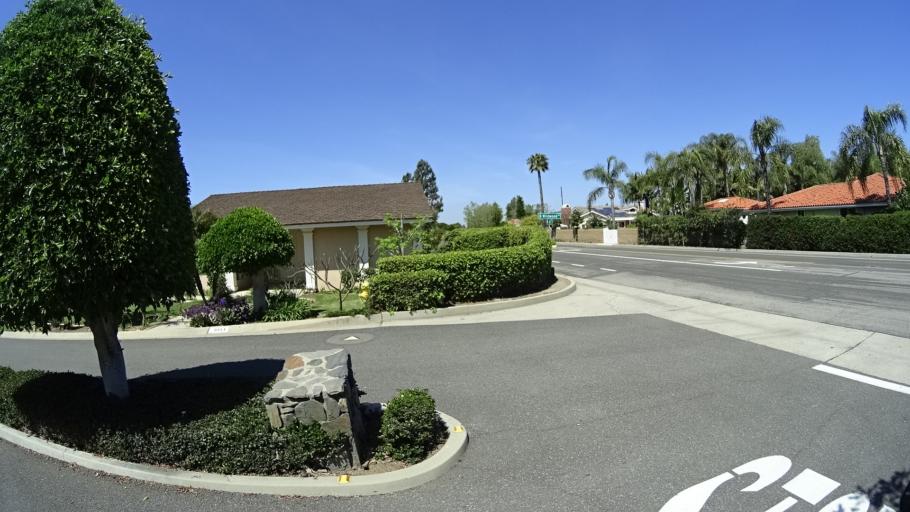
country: US
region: California
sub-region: Orange County
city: Villa Park
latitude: 33.8179
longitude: -117.8022
